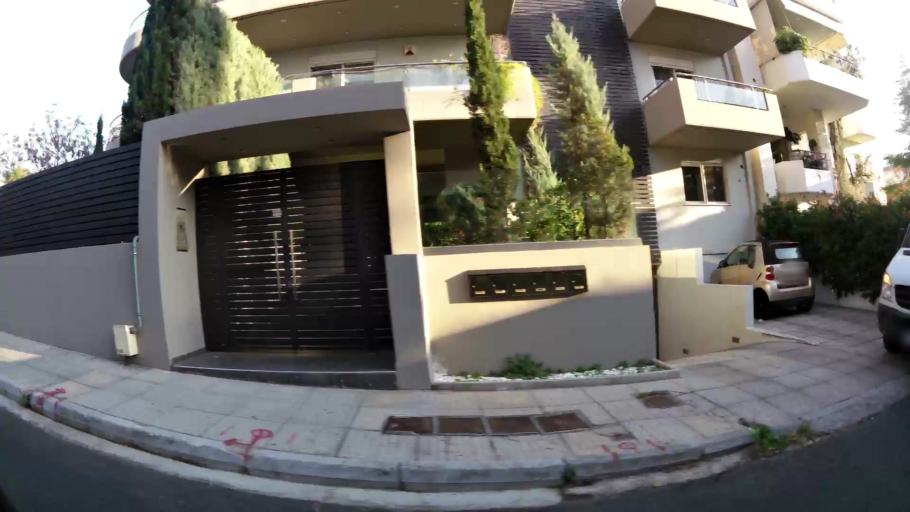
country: GR
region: Attica
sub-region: Nomarchia Athinas
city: Argyroupoli
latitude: 37.8980
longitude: 23.7688
